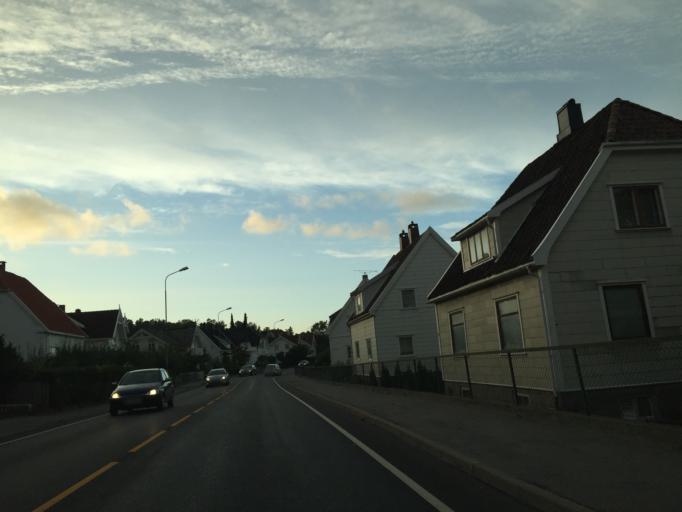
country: NO
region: Ostfold
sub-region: Fredrikstad
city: Fredrikstad
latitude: 59.2013
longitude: 10.9393
